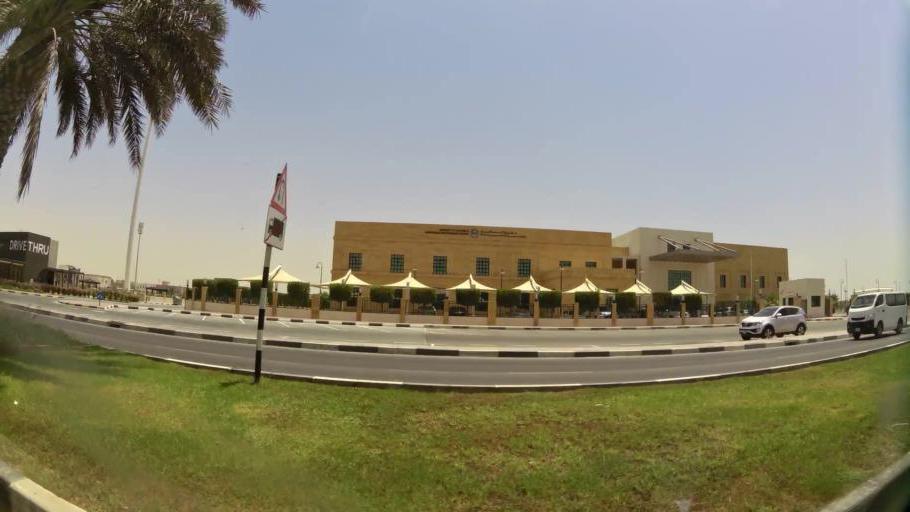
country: AE
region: Ajman
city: Ajman
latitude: 25.4143
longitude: 55.4980
